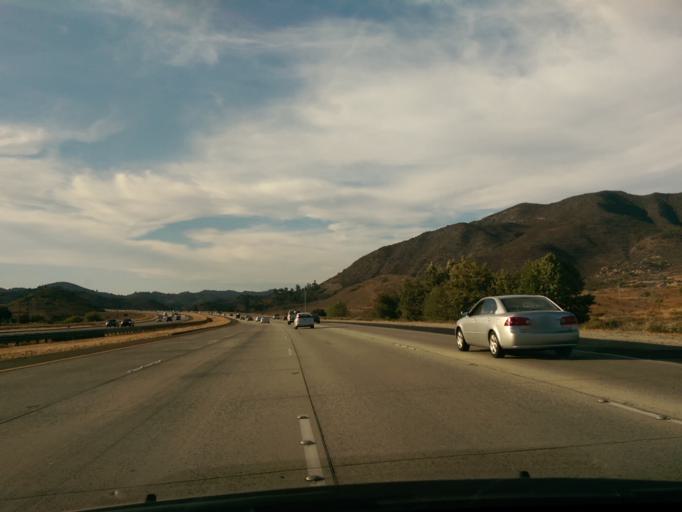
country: US
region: California
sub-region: San Diego County
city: Rainbow
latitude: 33.3551
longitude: -117.1588
